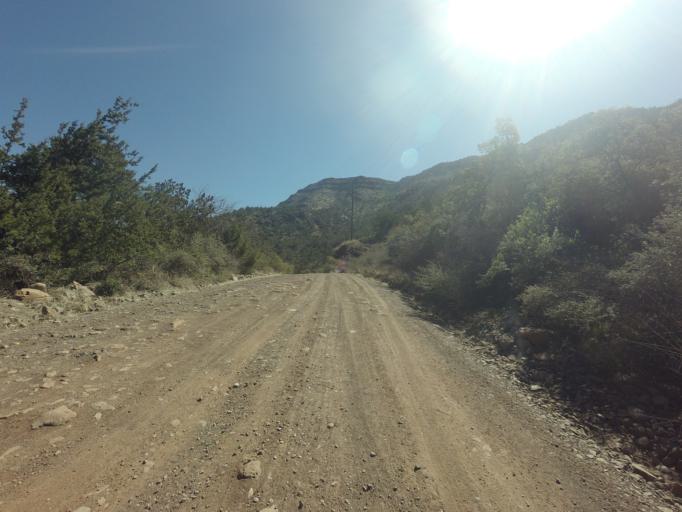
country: US
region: Arizona
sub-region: Gila County
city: Pine
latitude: 34.4001
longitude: -111.6216
